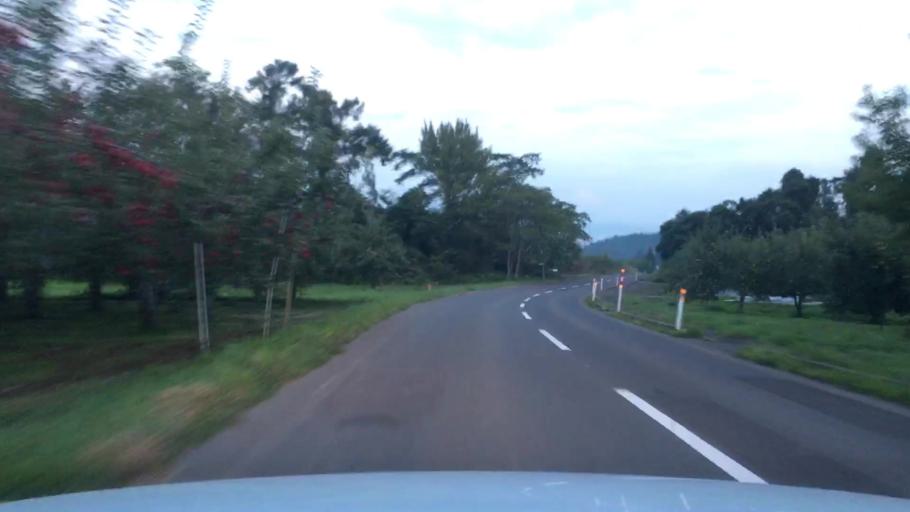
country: JP
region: Aomori
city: Hirosaki
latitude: 40.6769
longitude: 140.3799
